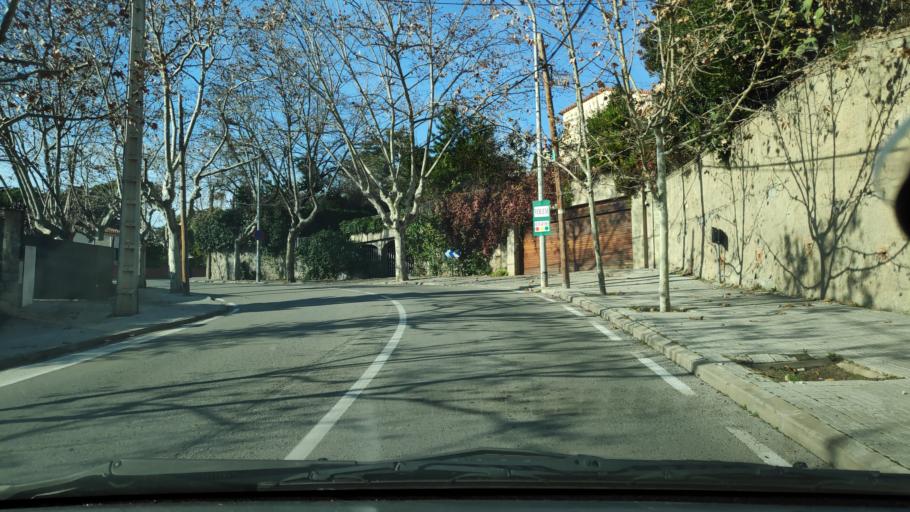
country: ES
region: Catalonia
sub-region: Provincia de Barcelona
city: Sant Quirze del Valles
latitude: 41.5024
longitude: 2.0906
